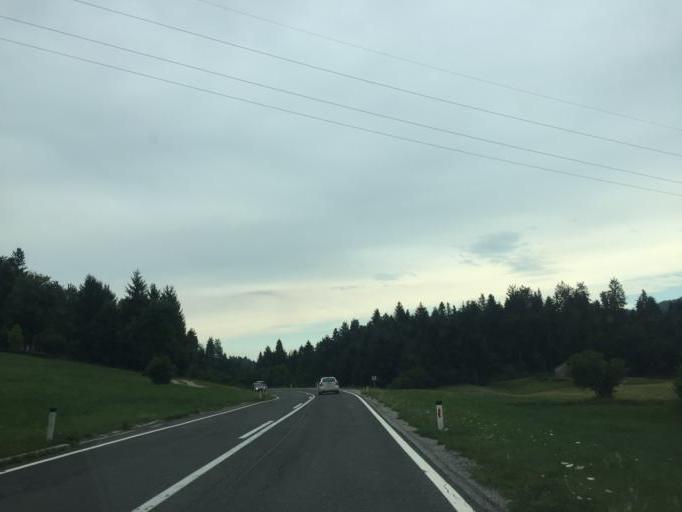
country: SI
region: Logatec
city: Logatec
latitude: 45.9016
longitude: 14.1796
